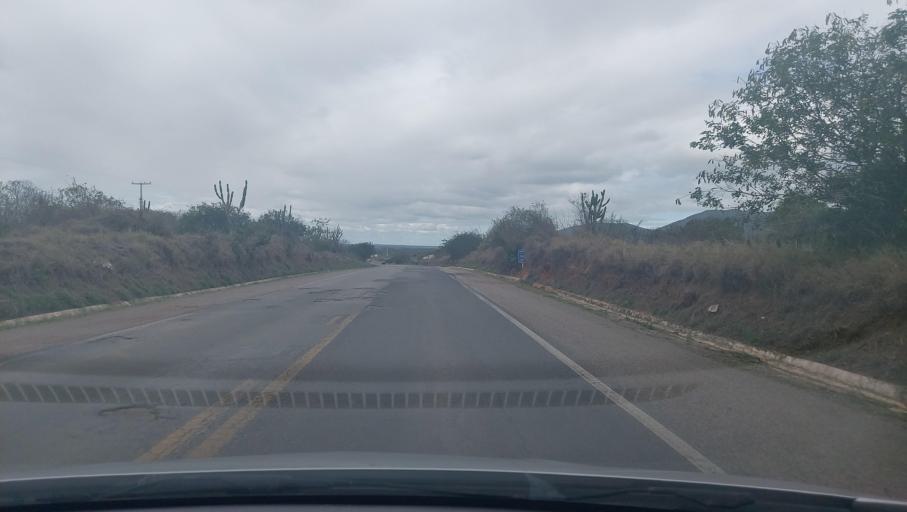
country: BR
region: Bahia
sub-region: Itaberaba
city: Itaberaba
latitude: -12.5198
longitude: -39.9523
